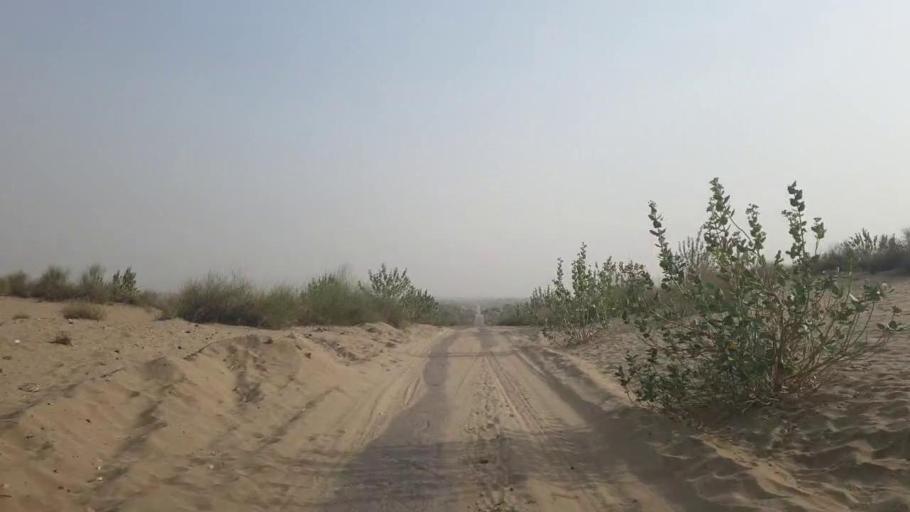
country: PK
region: Sindh
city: Chor
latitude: 25.4472
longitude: 69.9643
